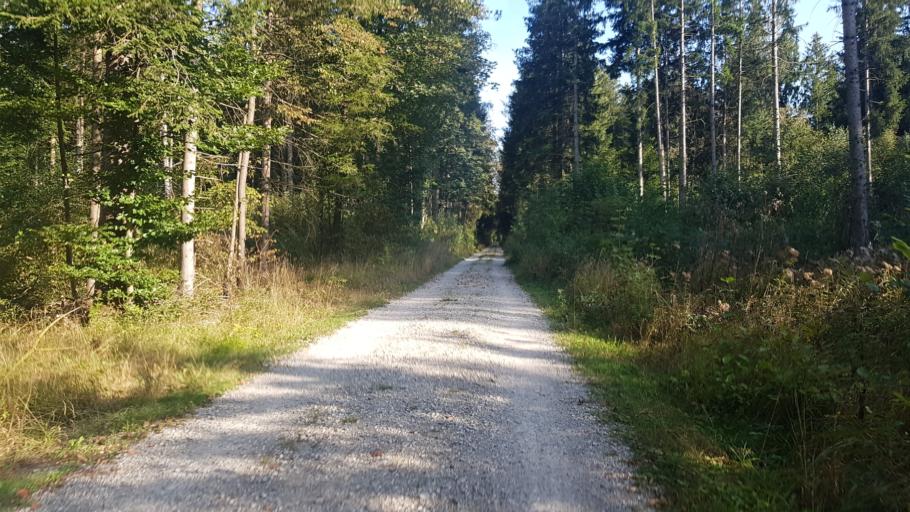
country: DE
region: Bavaria
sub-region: Upper Bavaria
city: Krailling
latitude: 48.0979
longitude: 11.3869
